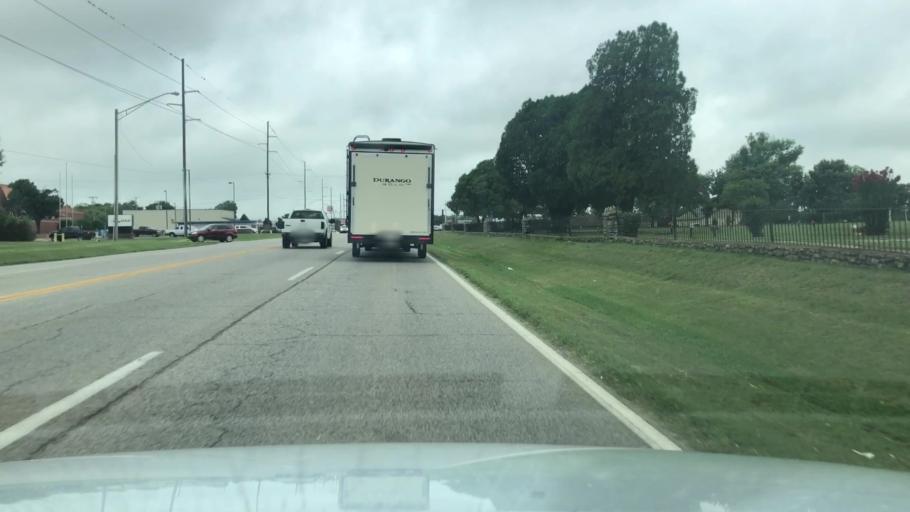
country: US
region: Oklahoma
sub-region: Washington County
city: Bartlesville
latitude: 36.7280
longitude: -95.9289
